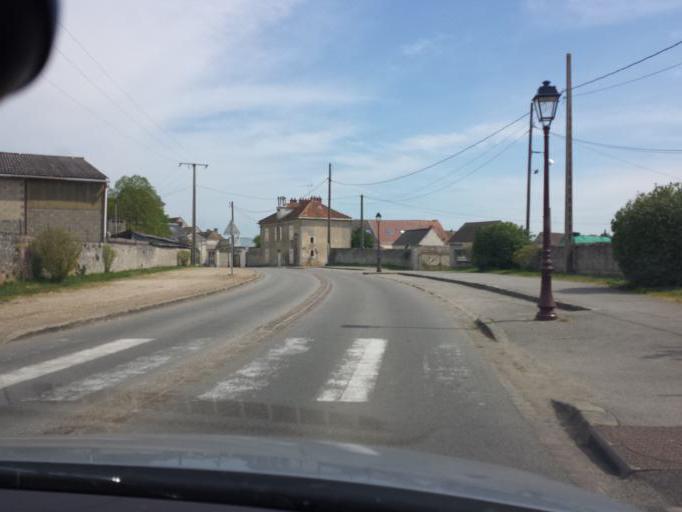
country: FR
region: Ile-de-France
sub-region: Departement des Yvelines
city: Villiers-Saint-Frederic
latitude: 48.8164
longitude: 1.8620
